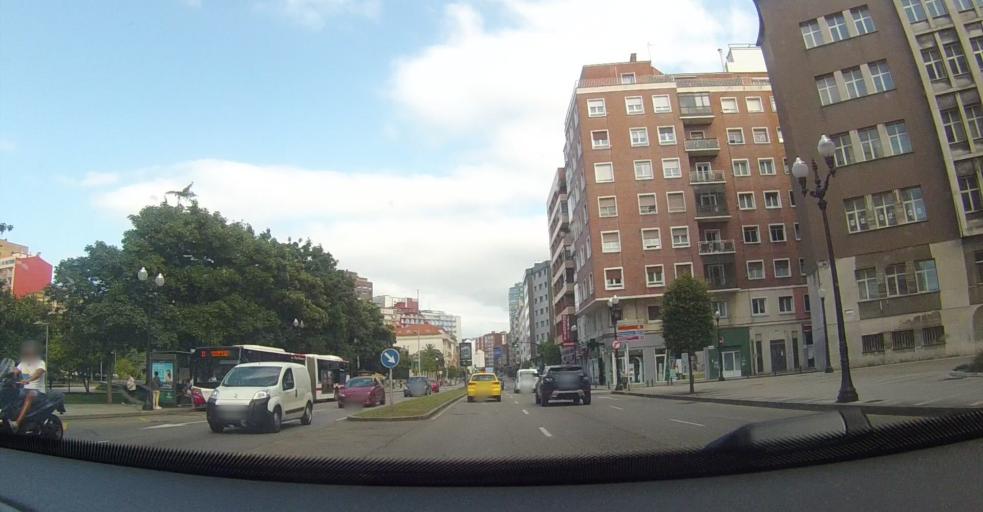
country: ES
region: Asturias
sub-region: Province of Asturias
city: Gijon
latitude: 43.5383
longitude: -5.6657
